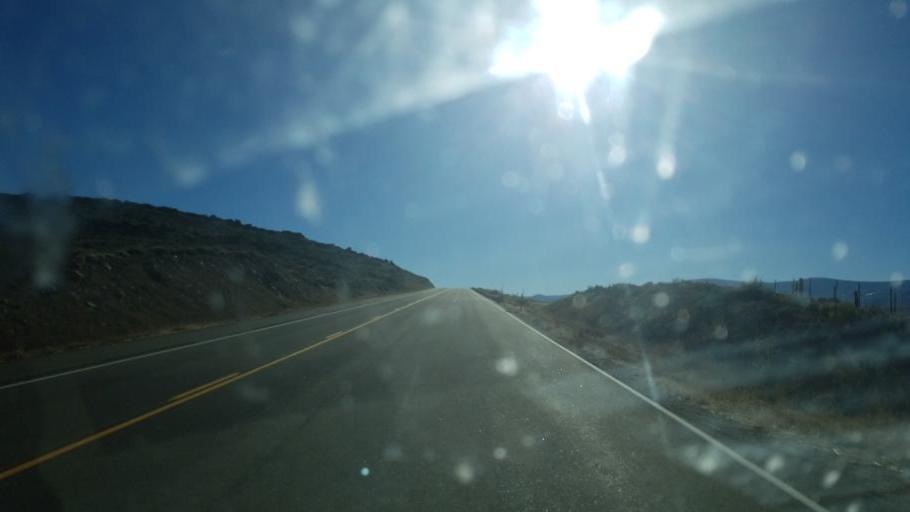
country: US
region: Colorado
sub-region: Gunnison County
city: Gunnison
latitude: 38.4614
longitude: -106.6291
